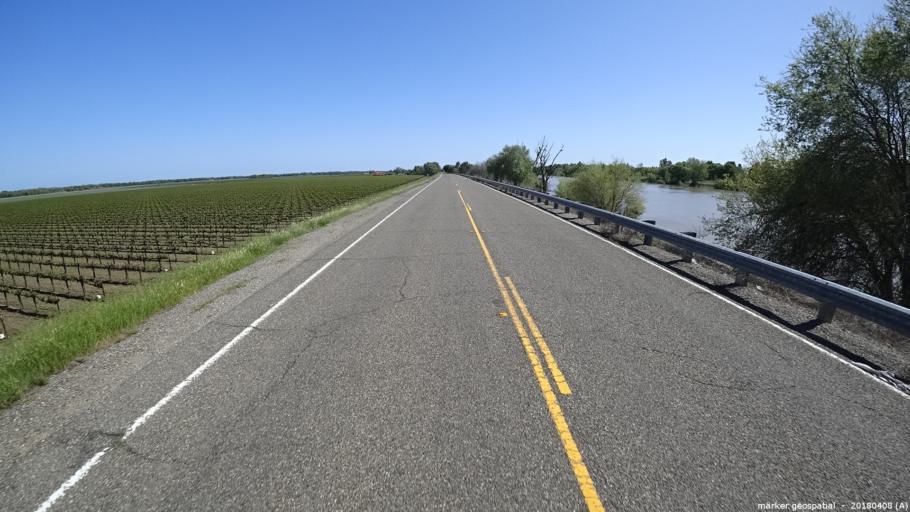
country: US
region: California
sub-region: Sacramento County
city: Parkway
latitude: 38.4263
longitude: -121.5291
